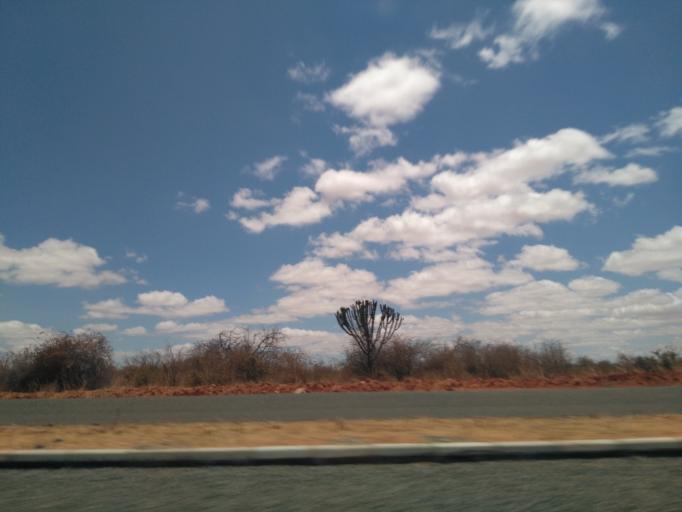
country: TZ
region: Dodoma
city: Kisasa
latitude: -6.1707
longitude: 35.8379
